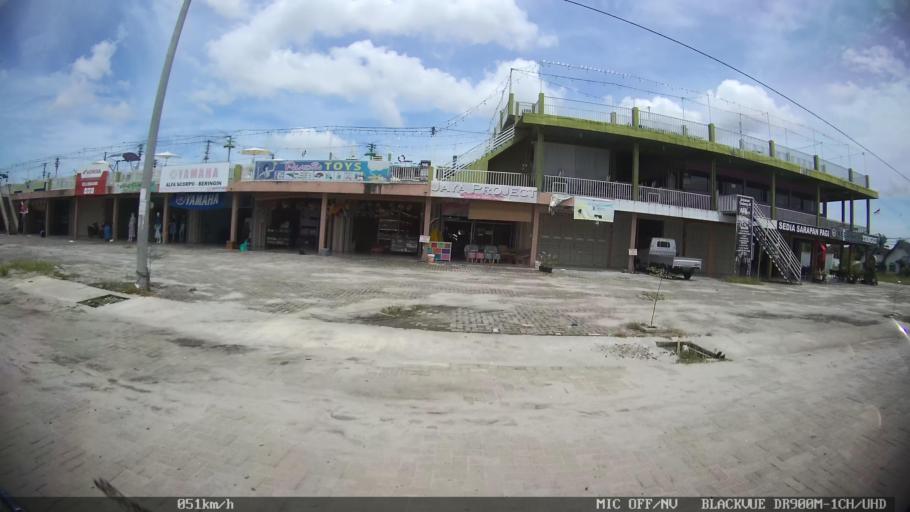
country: ID
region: North Sumatra
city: Percut
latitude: 3.5877
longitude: 98.8833
